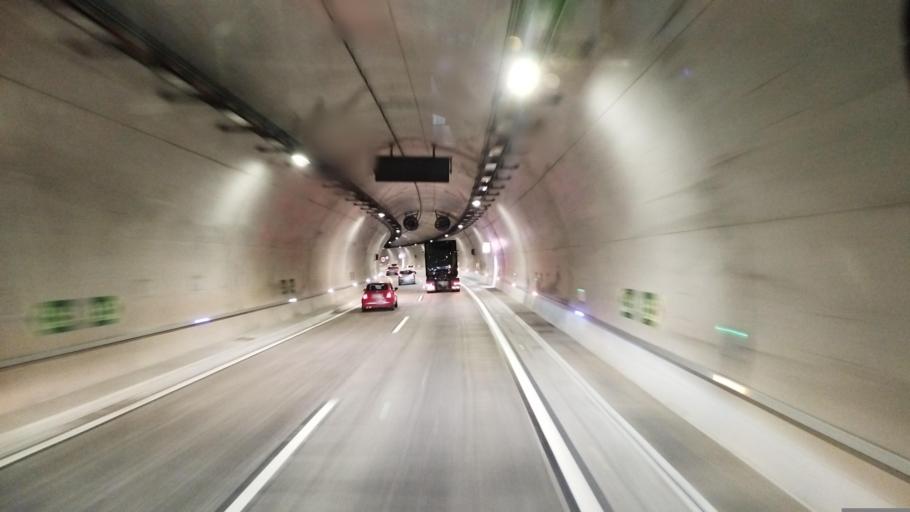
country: ES
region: Catalonia
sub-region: Provincia de Barcelona
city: Vallirana
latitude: 41.3854
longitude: 1.9406
